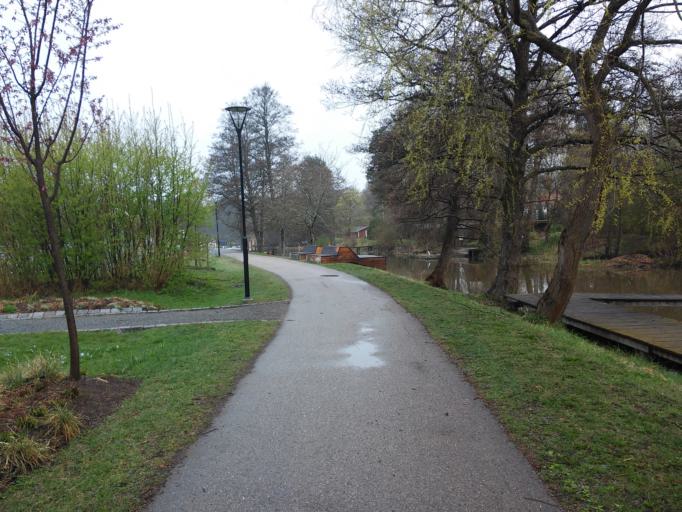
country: SE
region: Stockholm
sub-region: Osterakers Kommun
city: Akersberga
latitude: 59.4856
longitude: 18.2884
